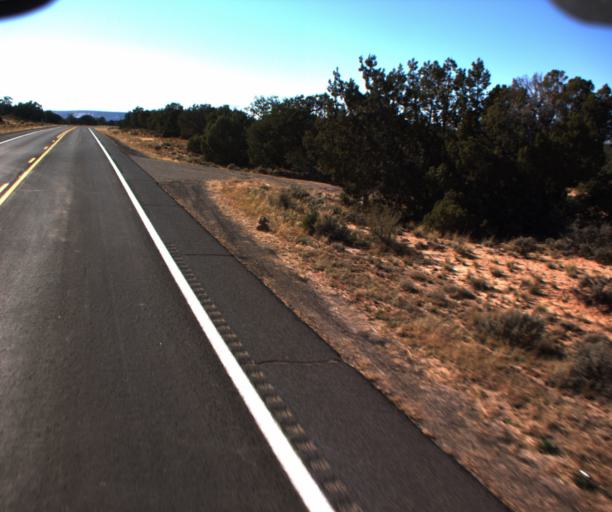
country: US
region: Arizona
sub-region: Coconino County
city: Kaibito
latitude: 36.5804
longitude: -110.8509
